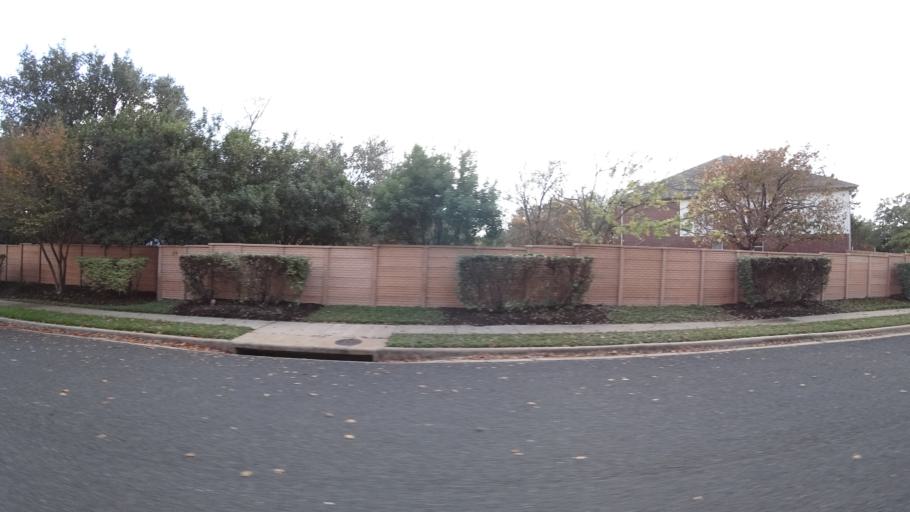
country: US
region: Texas
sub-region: Williamson County
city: Brushy Creek
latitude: 30.5087
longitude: -97.7342
